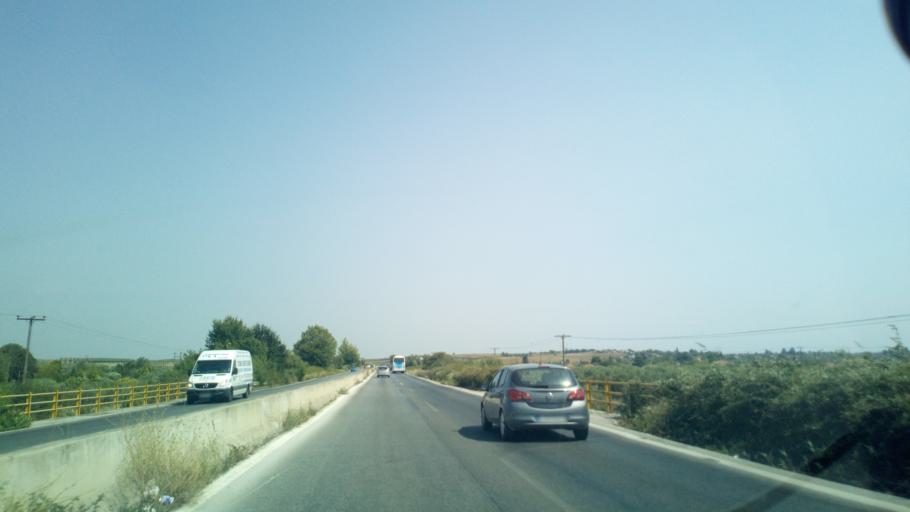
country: GR
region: Central Macedonia
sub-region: Nomos Chalkidikis
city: Nea Kallikrateia
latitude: 40.3094
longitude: 23.1202
